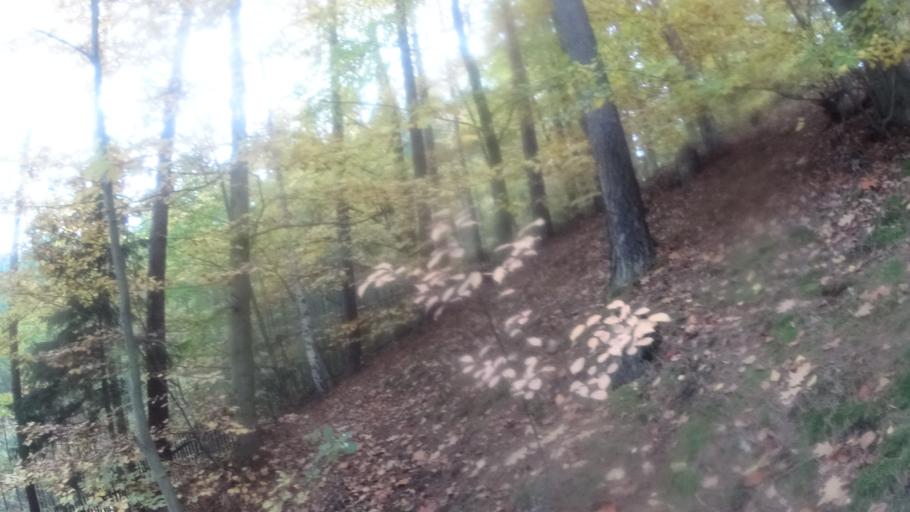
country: DE
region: Thuringia
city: Kleineutersdorf
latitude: 50.7666
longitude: 11.5805
